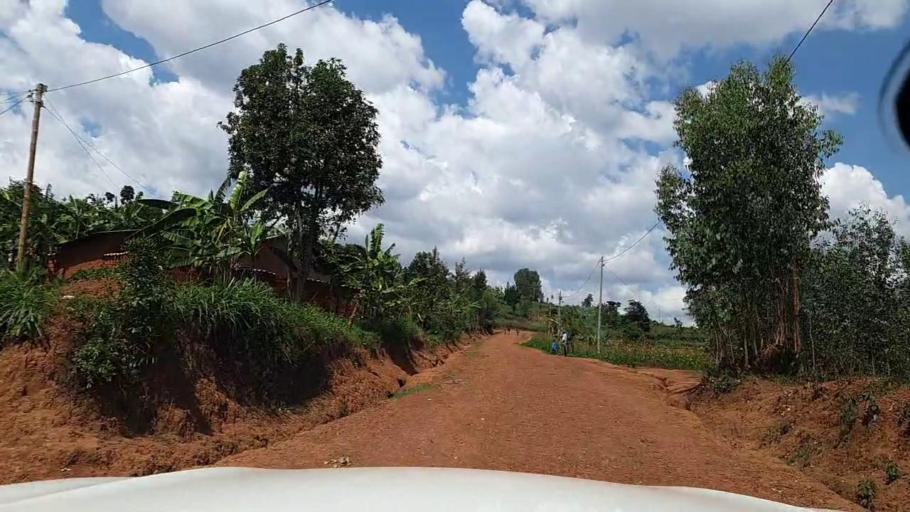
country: RW
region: Southern Province
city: Butare
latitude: -2.7485
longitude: 29.7034
